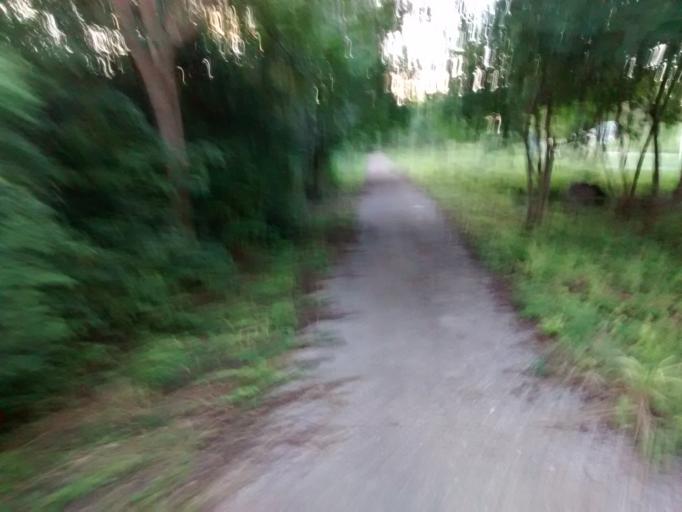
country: MX
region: Yucatan
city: Valladolid
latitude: 20.6934
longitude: -88.2254
